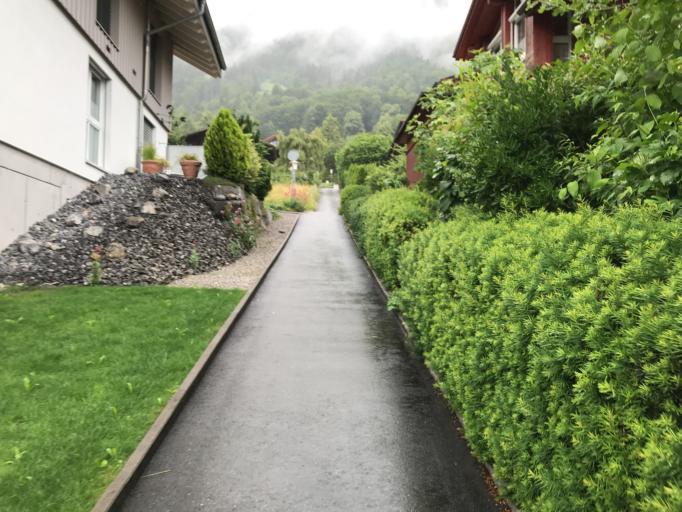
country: CH
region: Bern
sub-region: Interlaken-Oberhasli District
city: Ringgenberg
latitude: 46.7029
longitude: 7.8942
